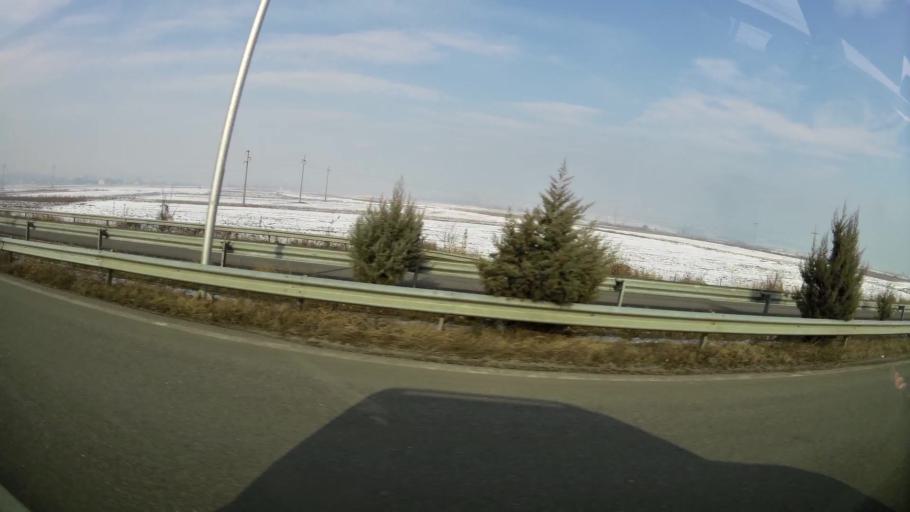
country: MK
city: Creshevo
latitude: 42.0311
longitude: 21.5038
